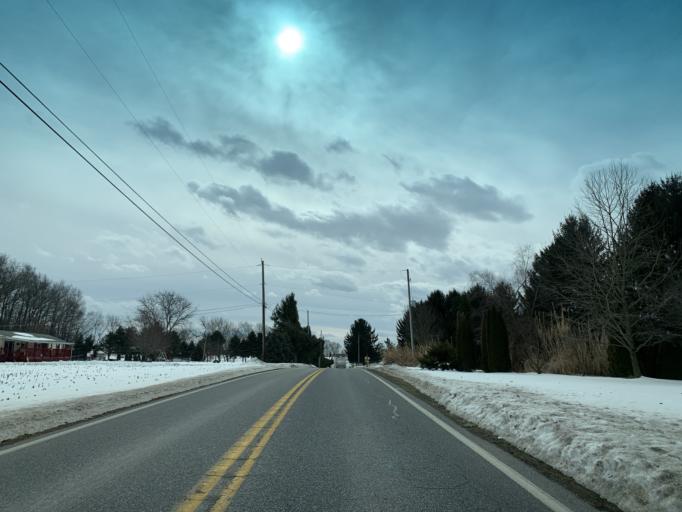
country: US
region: Pennsylvania
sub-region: York County
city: Shrewsbury
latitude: 39.7879
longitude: -76.6373
